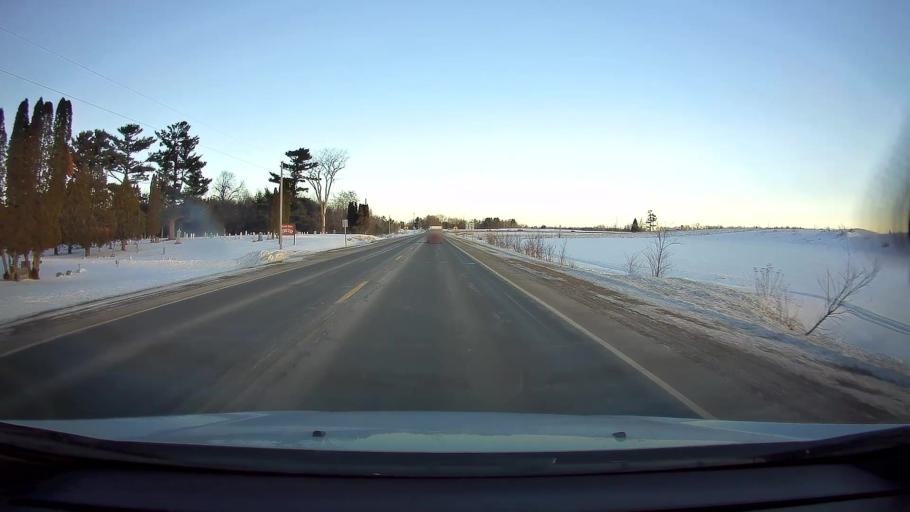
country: US
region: Wisconsin
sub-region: Barron County
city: Turtle Lake
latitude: 45.3907
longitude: -92.1666
